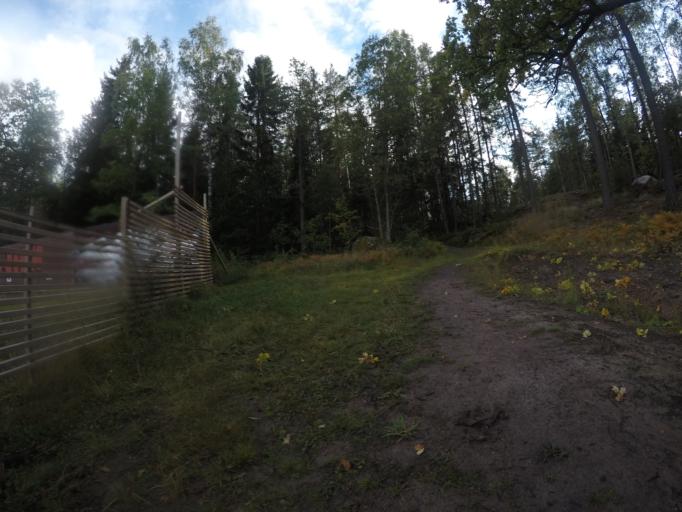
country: SE
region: Vaestmanland
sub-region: Vasteras
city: Vasteras
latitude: 59.6333
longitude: 16.5223
